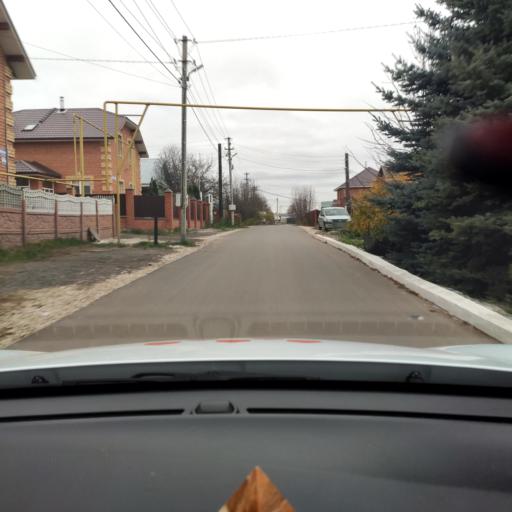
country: RU
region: Tatarstan
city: Vysokaya Gora
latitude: 55.8736
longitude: 49.2560
